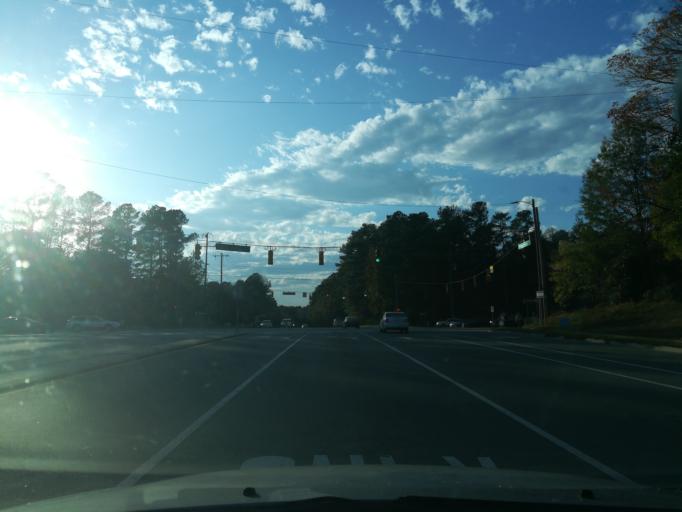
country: US
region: North Carolina
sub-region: Orange County
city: Chapel Hill
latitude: 35.9641
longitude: -79.0577
